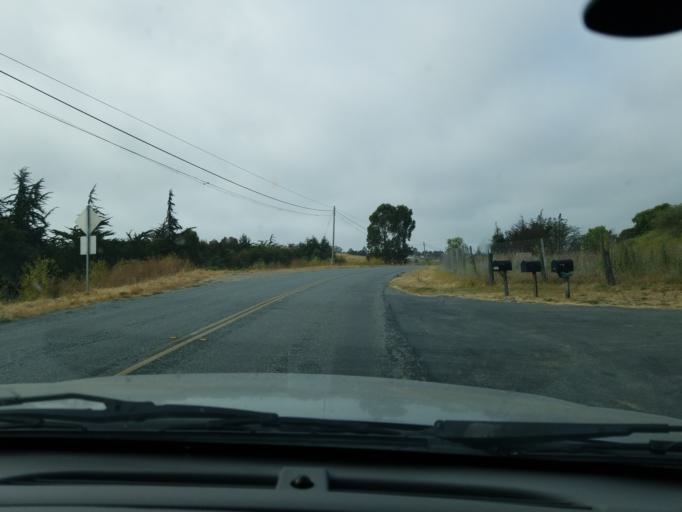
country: US
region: California
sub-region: Monterey County
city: Las Lomas
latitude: 36.8592
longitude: -121.7547
